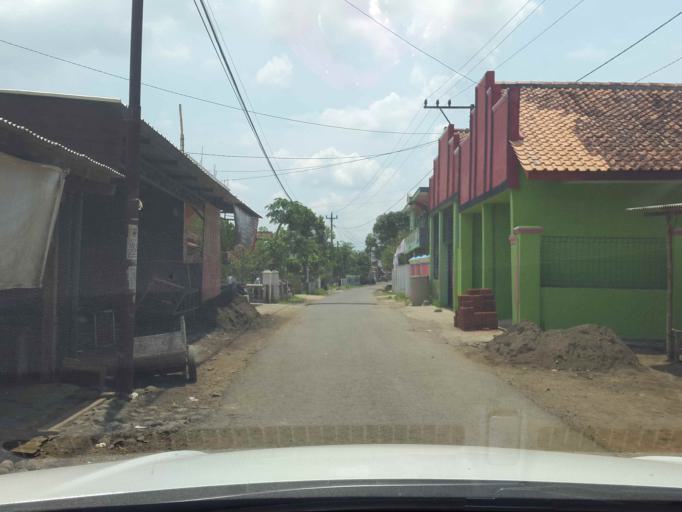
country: ID
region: Central Java
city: Wanareja
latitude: -7.3370
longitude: 108.6835
